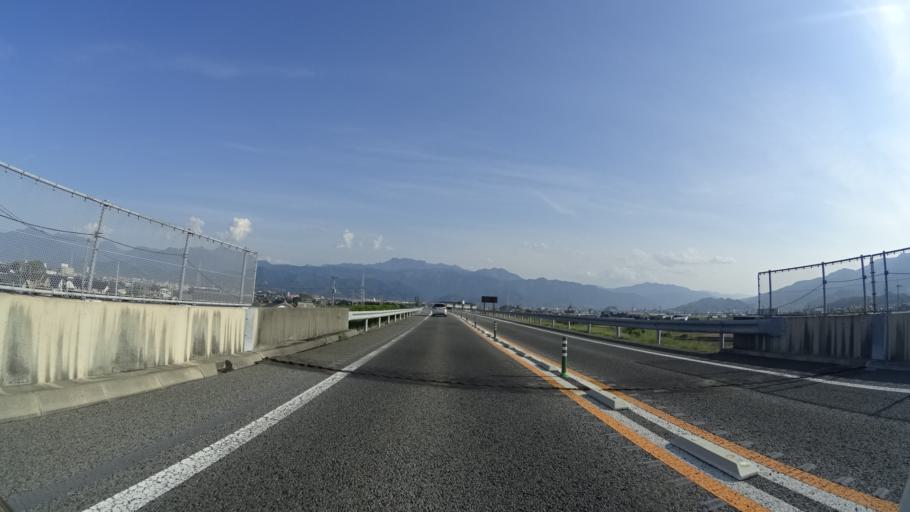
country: JP
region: Ehime
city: Saijo
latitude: 33.9373
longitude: 133.0693
